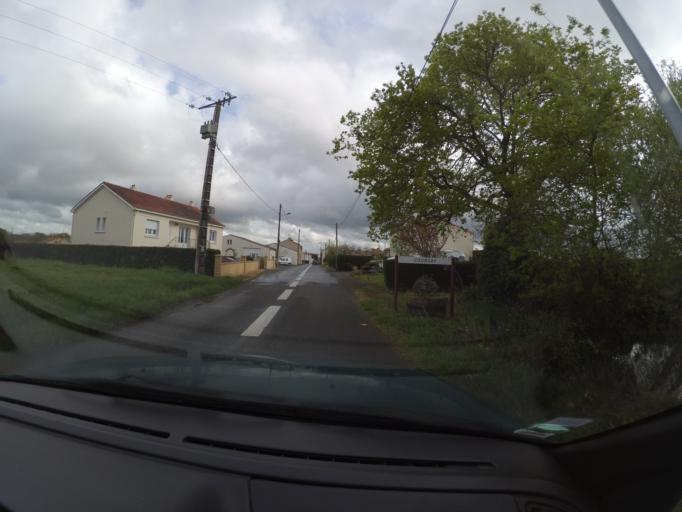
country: FR
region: Pays de la Loire
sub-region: Departement de la Loire-Atlantique
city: Monnieres
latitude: 47.1138
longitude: -1.3628
